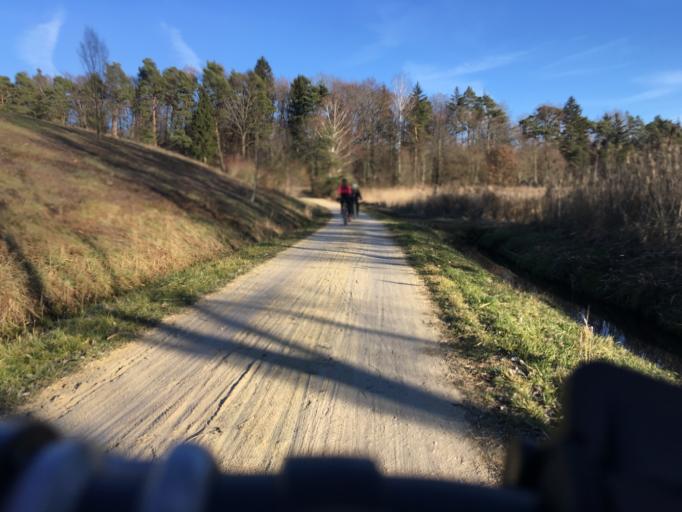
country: DE
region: Baden-Wuerttemberg
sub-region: Freiburg Region
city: Moos
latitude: 47.7200
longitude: 8.9207
